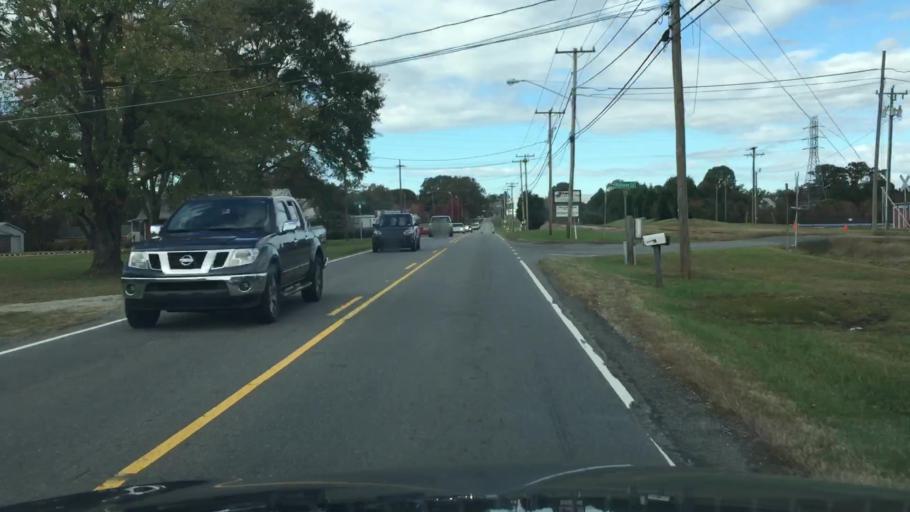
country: US
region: North Carolina
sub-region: Iredell County
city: Mooresville
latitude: 35.6068
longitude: -80.8156
